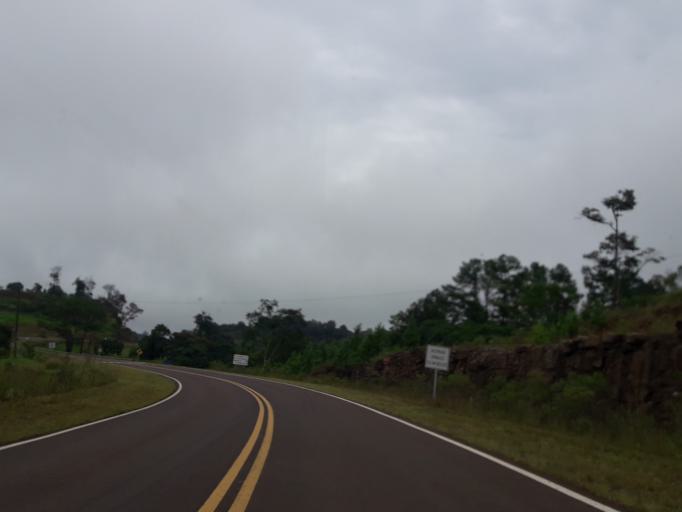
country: AR
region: Misiones
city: Bernardo de Irigoyen
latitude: -26.3964
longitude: -53.8154
